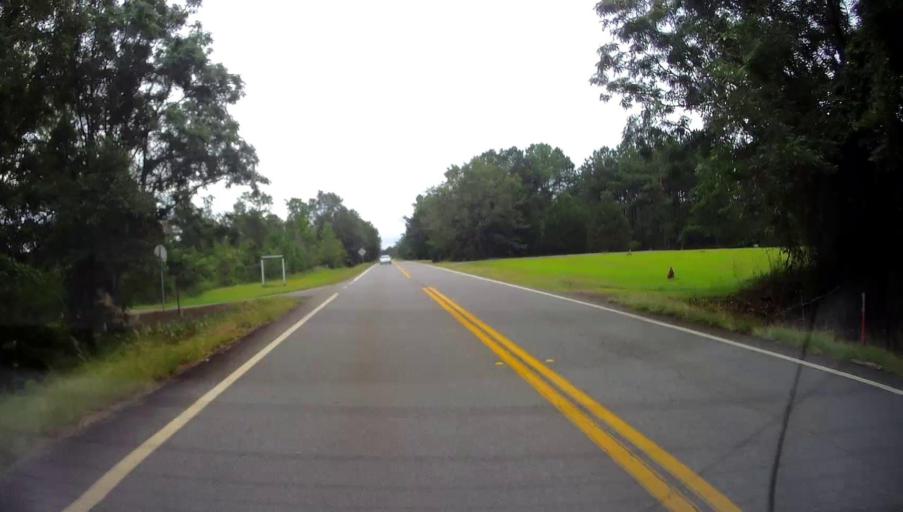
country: US
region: Georgia
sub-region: Marion County
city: Buena Vista
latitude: 32.2759
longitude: -84.4350
